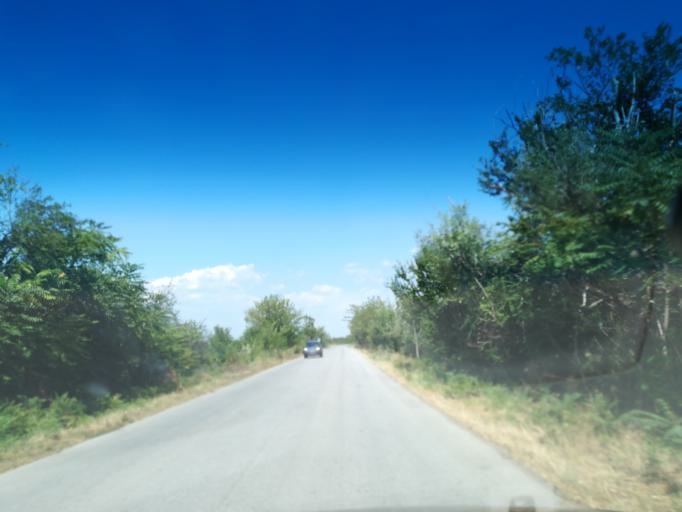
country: BG
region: Stara Zagora
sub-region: Obshtina Chirpan
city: Chirpan
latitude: 42.0694
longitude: 25.1790
